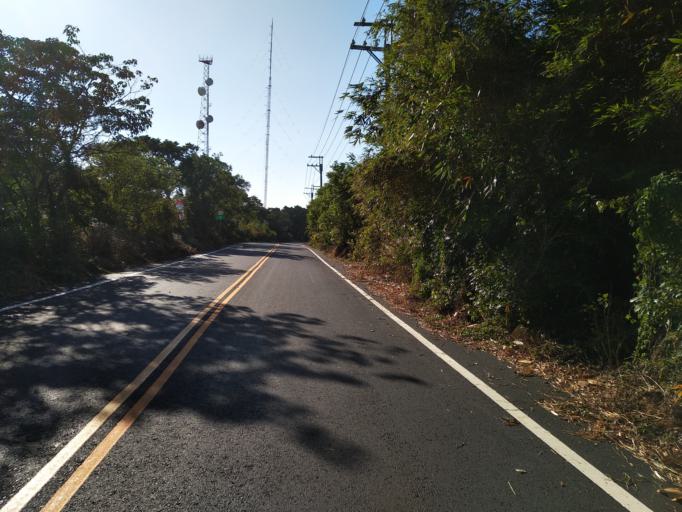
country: TW
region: Taiwan
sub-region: Hsinchu
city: Zhubei
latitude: 24.8721
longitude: 121.0682
